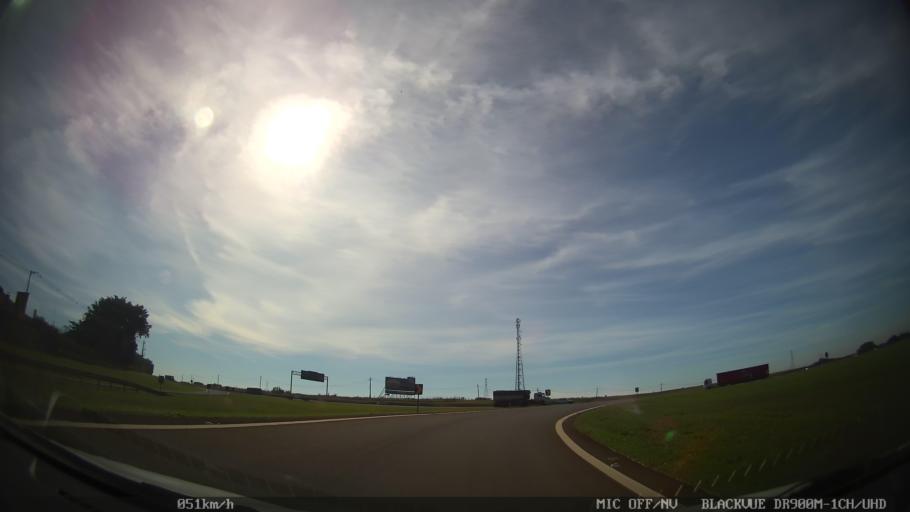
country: BR
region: Sao Paulo
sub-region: Cordeiropolis
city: Cordeiropolis
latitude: -22.5007
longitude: -47.4007
